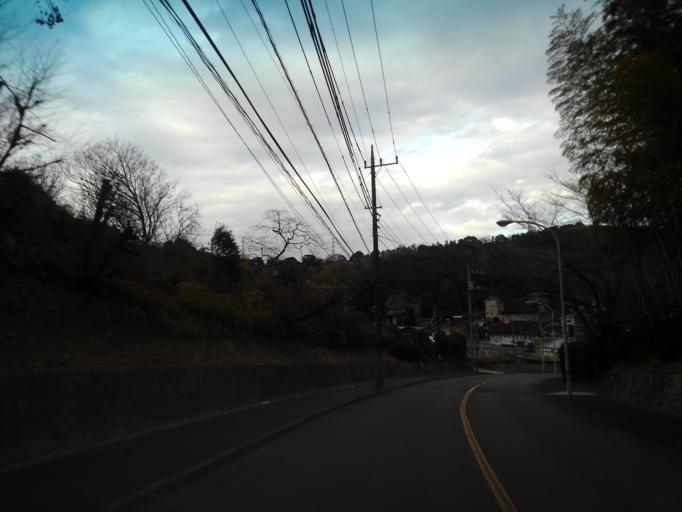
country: JP
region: Tokyo
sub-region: Machida-shi
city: Machida
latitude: 35.6022
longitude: 139.4437
